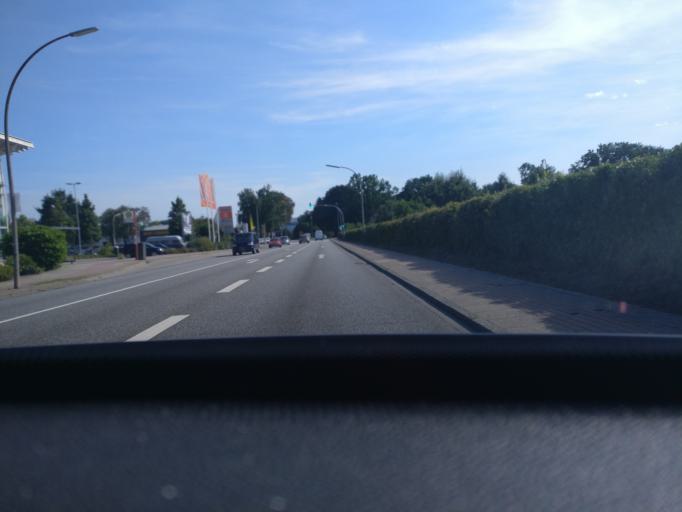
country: DE
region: Schleswig-Holstein
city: Norderstedt
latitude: 53.6684
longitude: 9.9710
